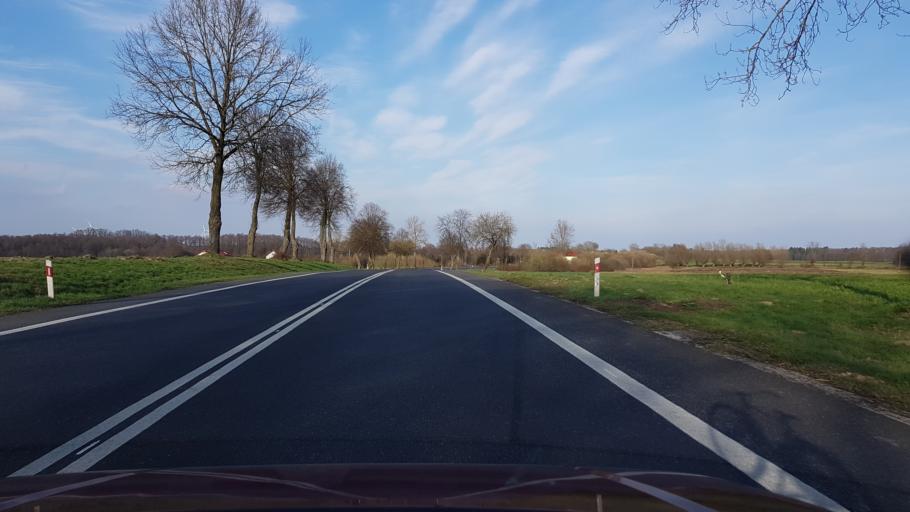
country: PL
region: West Pomeranian Voivodeship
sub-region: Powiat bialogardzki
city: Karlino
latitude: 54.0044
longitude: 15.7831
